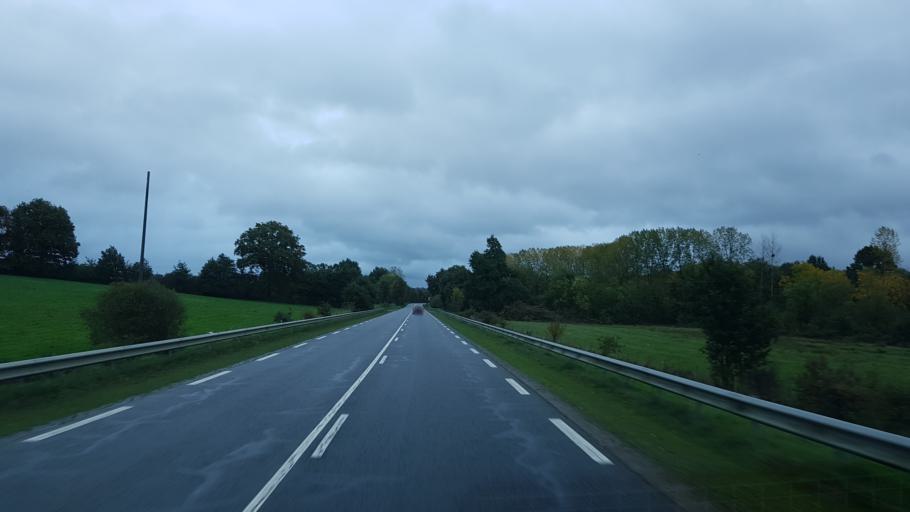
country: FR
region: Brittany
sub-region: Departement d'Ille-et-Vilaine
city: Vitre
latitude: 48.1316
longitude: -1.2016
